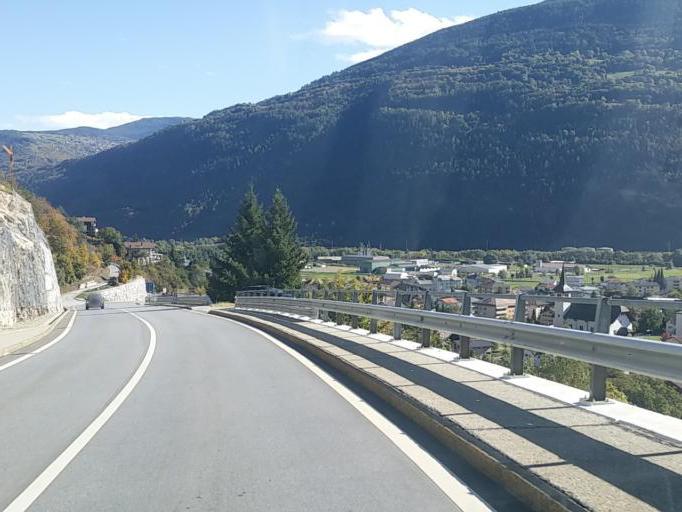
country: CH
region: Valais
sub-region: Leuk District
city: Gampel
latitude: 46.3182
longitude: 7.7453
